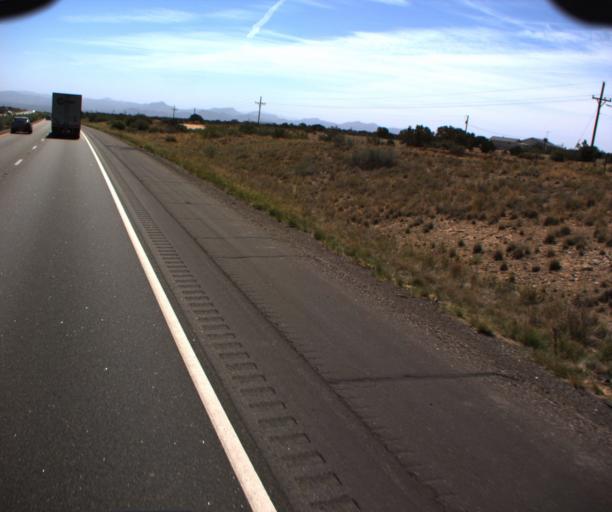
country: US
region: Arizona
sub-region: Mohave County
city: New Kingman-Butler
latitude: 35.1711
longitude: -113.7752
